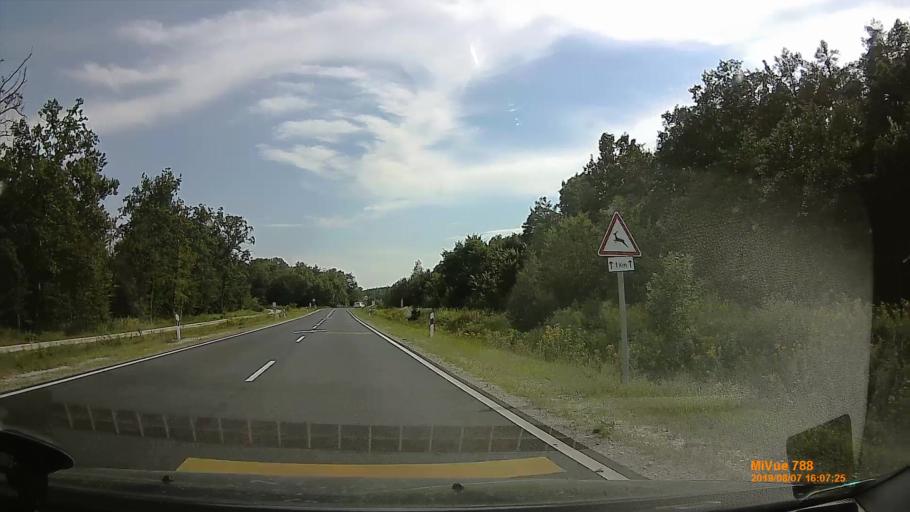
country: HU
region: Zala
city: Zalalovo
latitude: 46.9211
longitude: 16.5996
